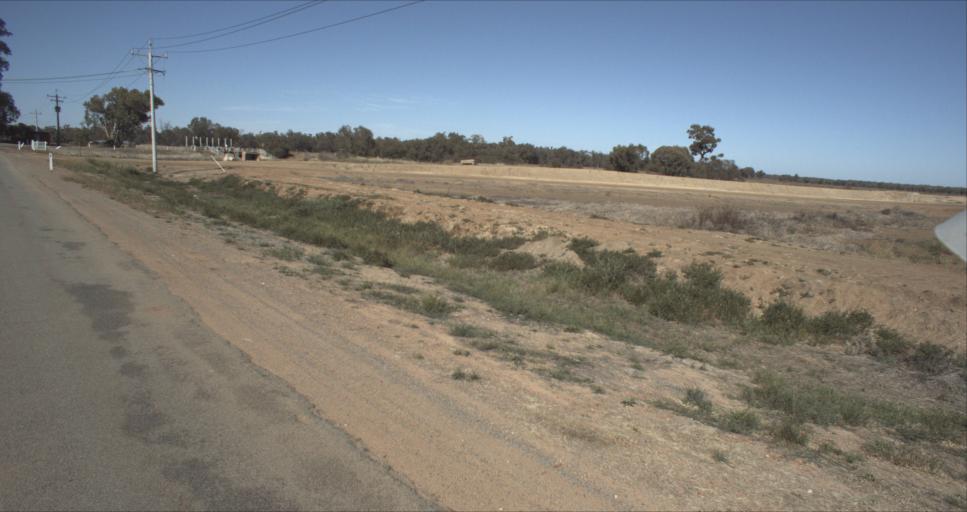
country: AU
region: New South Wales
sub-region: Leeton
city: Leeton
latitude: -34.6044
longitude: 146.2570
